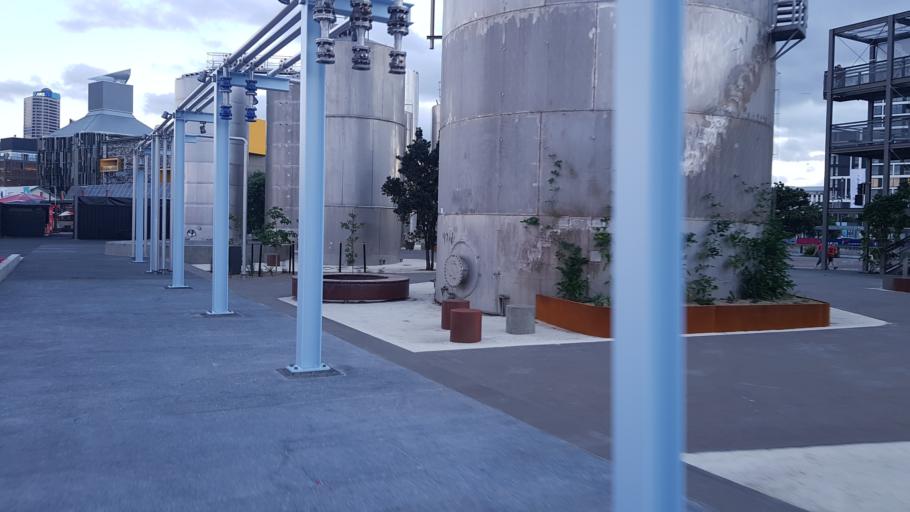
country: NZ
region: Auckland
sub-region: Auckland
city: Auckland
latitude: -36.8397
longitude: 174.7557
